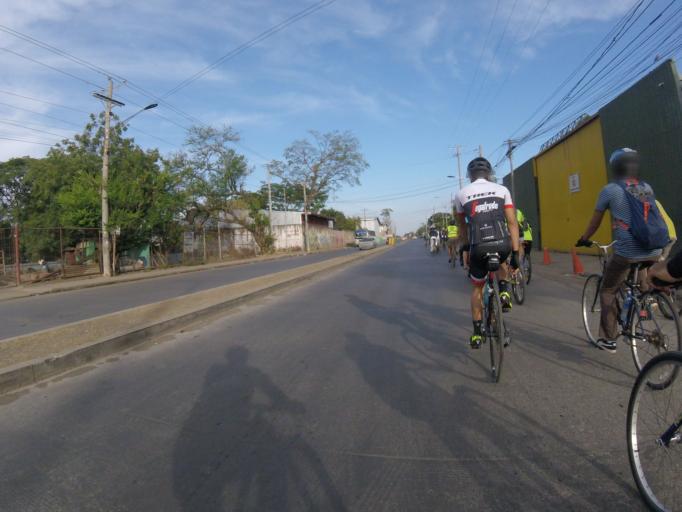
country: NI
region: Managua
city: Managua
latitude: 12.1256
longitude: -86.2038
